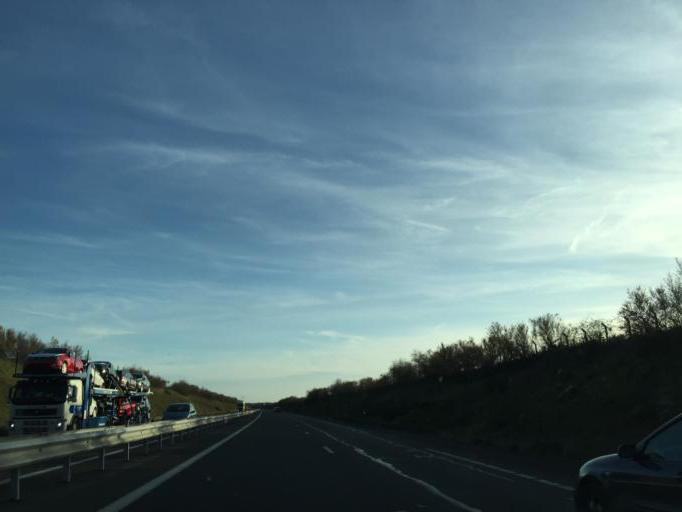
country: FR
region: Rhone-Alpes
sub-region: Departement de l'Isere
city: Janneyrias
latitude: 45.7288
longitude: 5.0957
